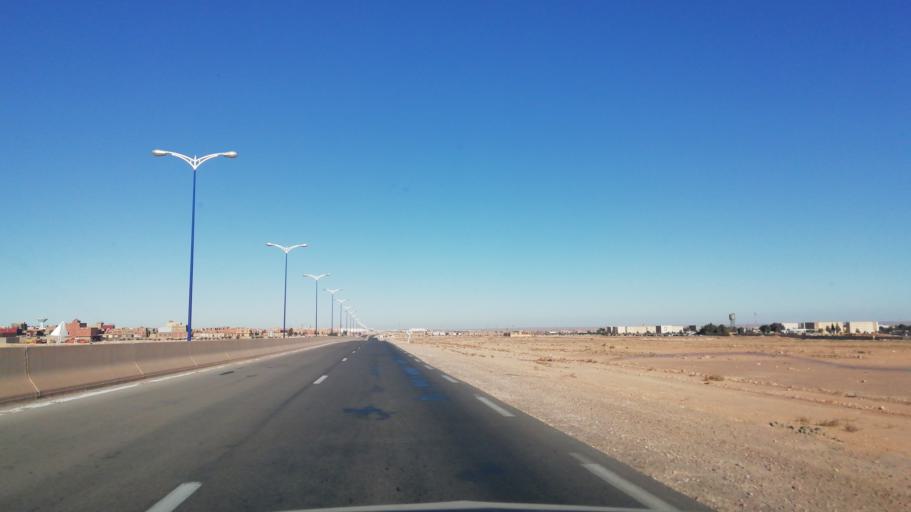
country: DZ
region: Wilaya de Naama
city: Naama
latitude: 33.5311
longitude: -0.2705
